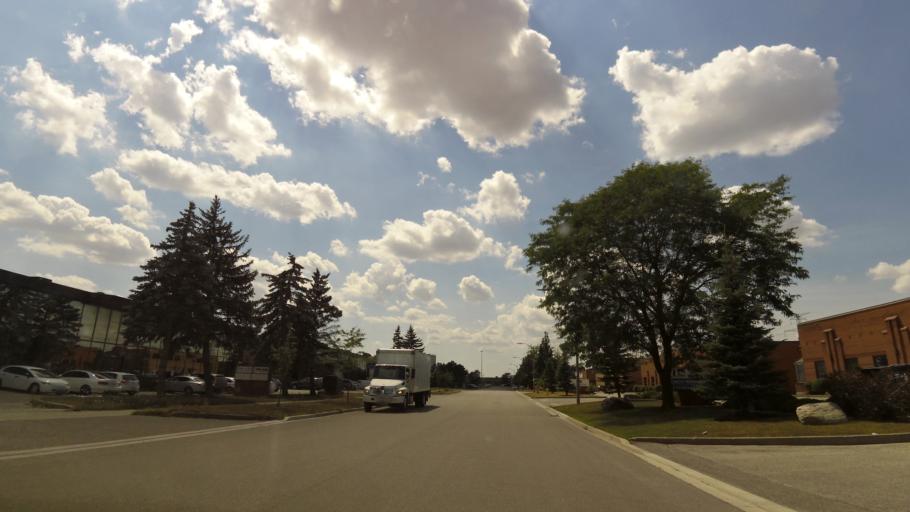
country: CA
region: Ontario
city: Concord
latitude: 43.7770
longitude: -79.5286
